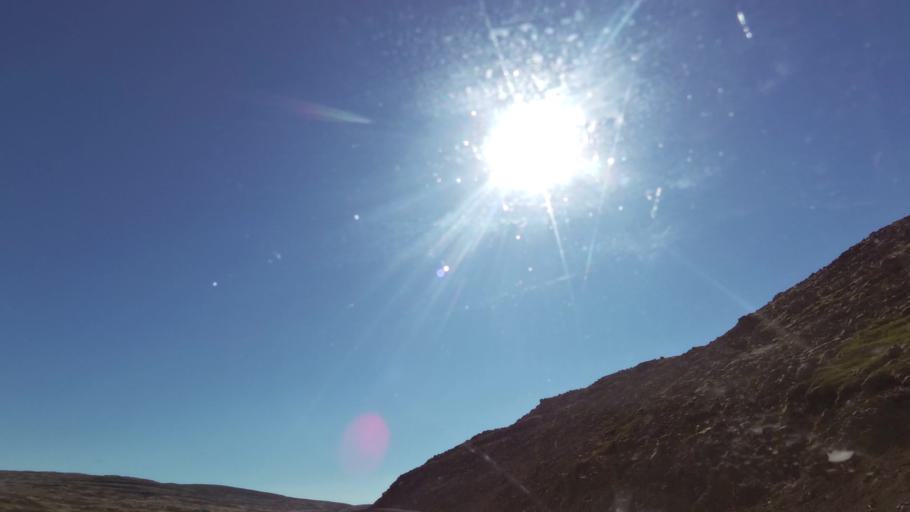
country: IS
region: West
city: Olafsvik
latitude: 65.5570
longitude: -24.1941
